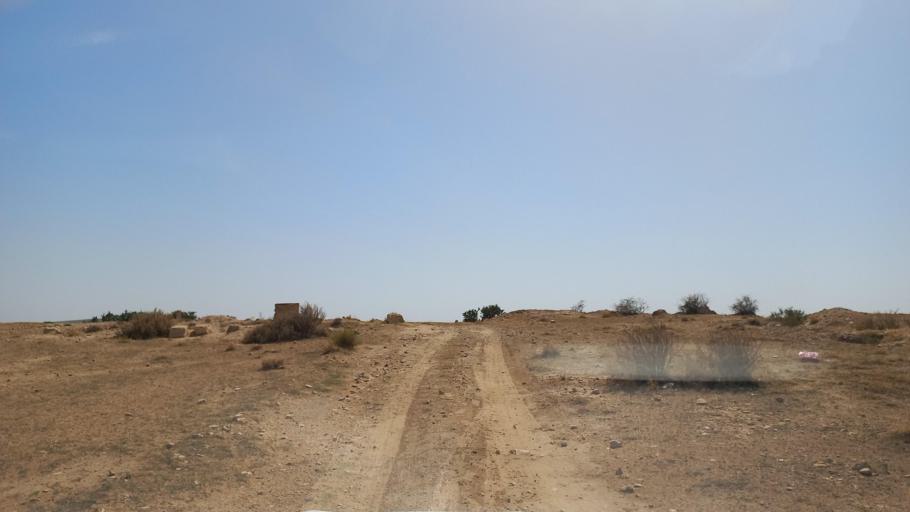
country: TN
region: Al Qasrayn
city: Kasserine
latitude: 35.2253
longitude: 9.0357
